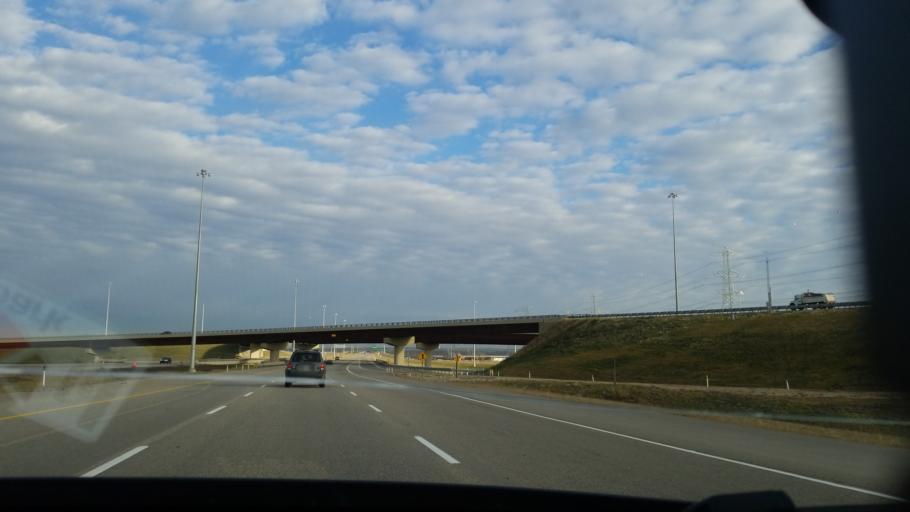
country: CA
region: Alberta
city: Sherwood Park
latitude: 53.5677
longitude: -113.3445
